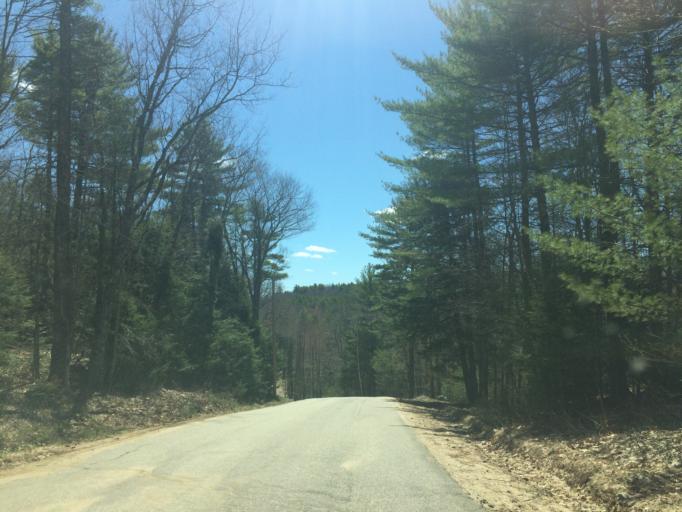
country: US
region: Maine
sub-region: Oxford County
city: Porter
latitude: 43.7920
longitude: -70.8739
